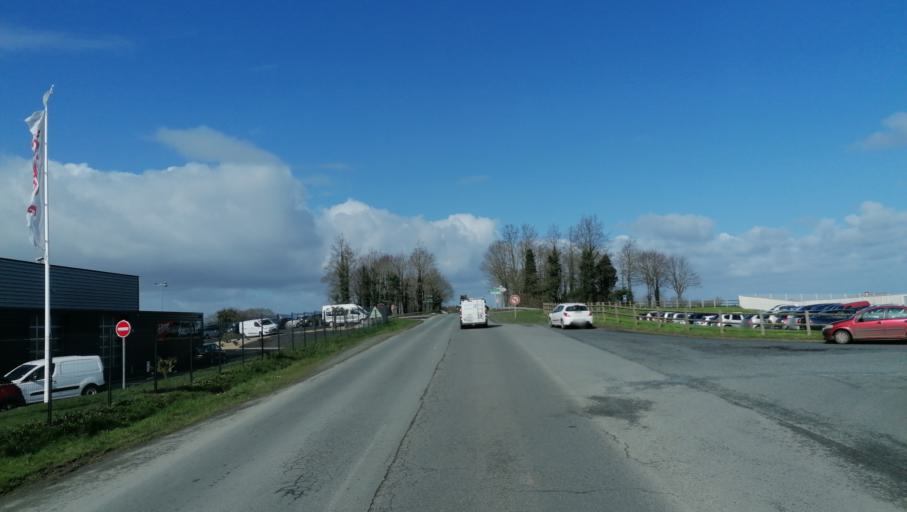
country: FR
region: Brittany
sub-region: Departement des Cotes-d'Armor
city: Tremuson
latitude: 48.5292
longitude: -2.8565
